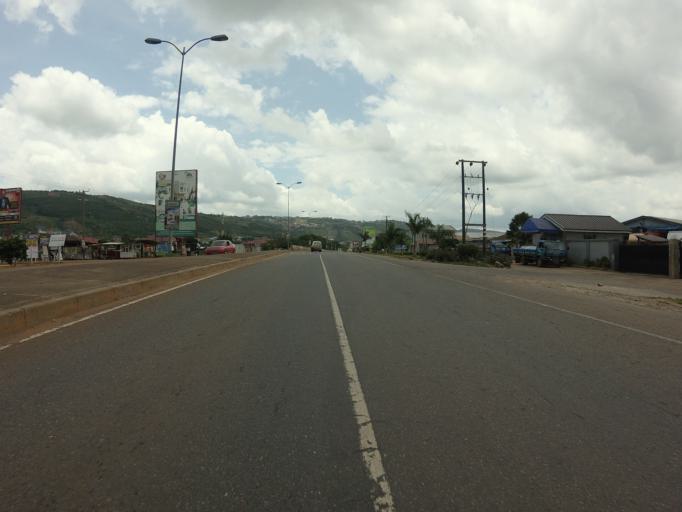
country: GH
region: Eastern
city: Aburi
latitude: 5.7732
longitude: -0.1810
